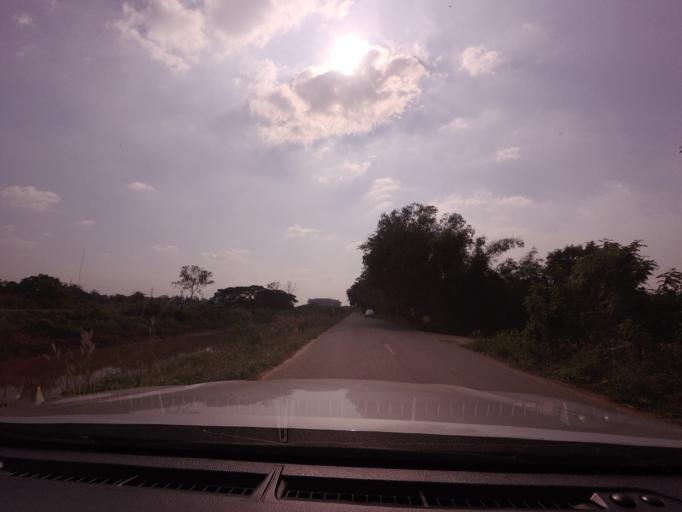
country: TH
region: Phitsanulok
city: Phitsanulok
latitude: 16.7928
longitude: 100.2063
